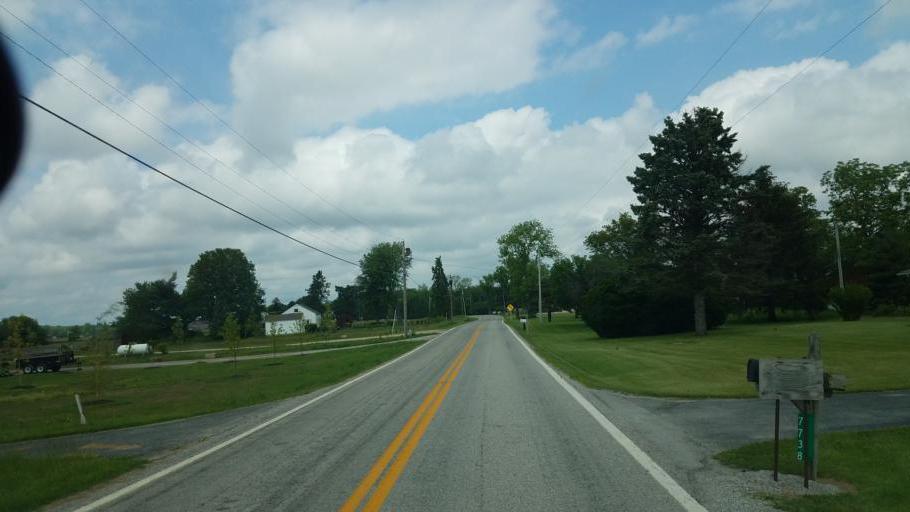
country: US
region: Ohio
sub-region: Marion County
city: Prospect
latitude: 40.4395
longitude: -83.1943
